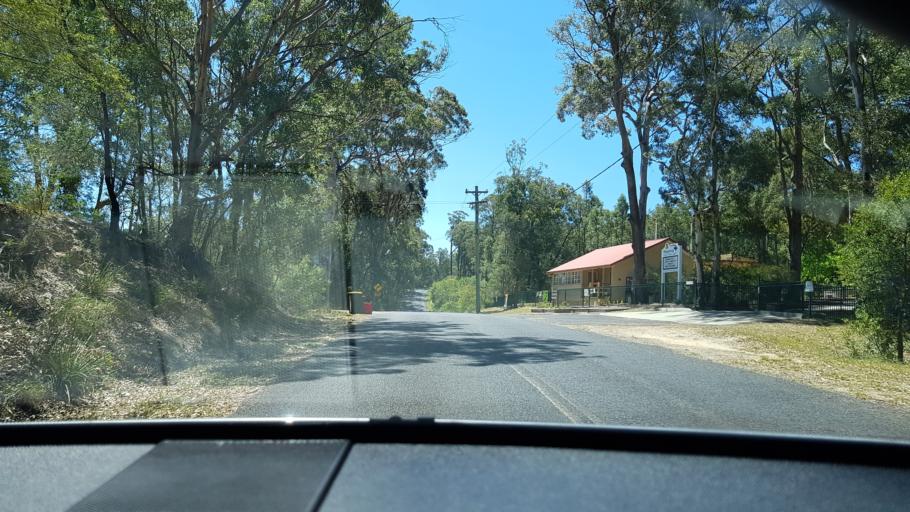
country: AU
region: New South Wales
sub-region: Blue Mountains Municipality
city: Katoomba
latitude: -33.7158
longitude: 150.2318
